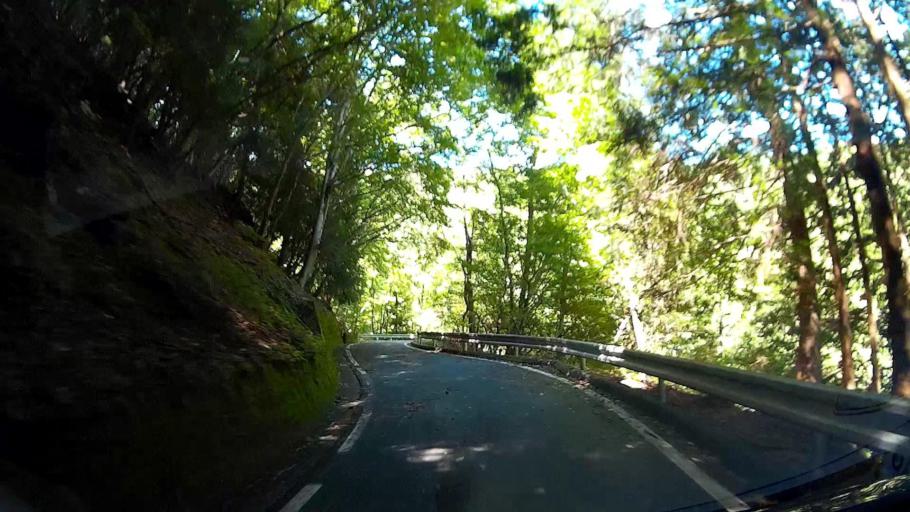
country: JP
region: Shizuoka
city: Shizuoka-shi
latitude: 35.1966
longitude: 138.2646
